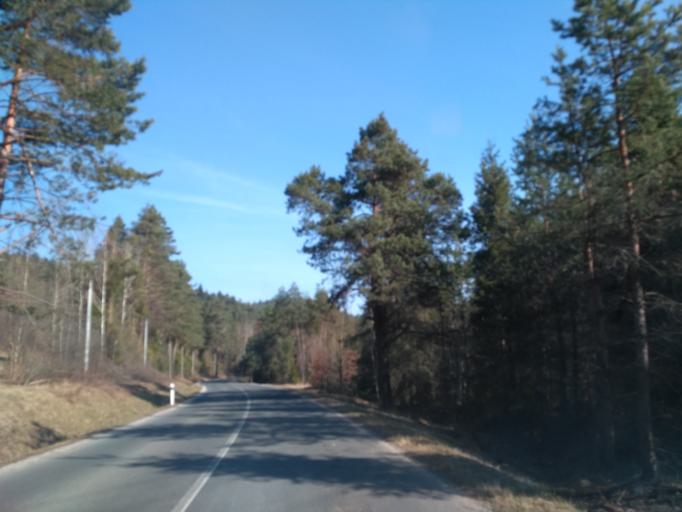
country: SK
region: Kosicky
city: Medzev
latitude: 48.7575
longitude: 20.7765
